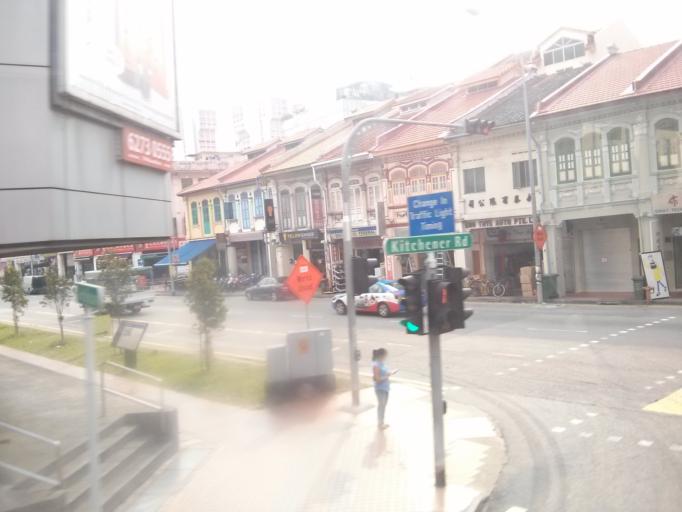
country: SG
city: Singapore
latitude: 1.3091
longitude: 103.8579
